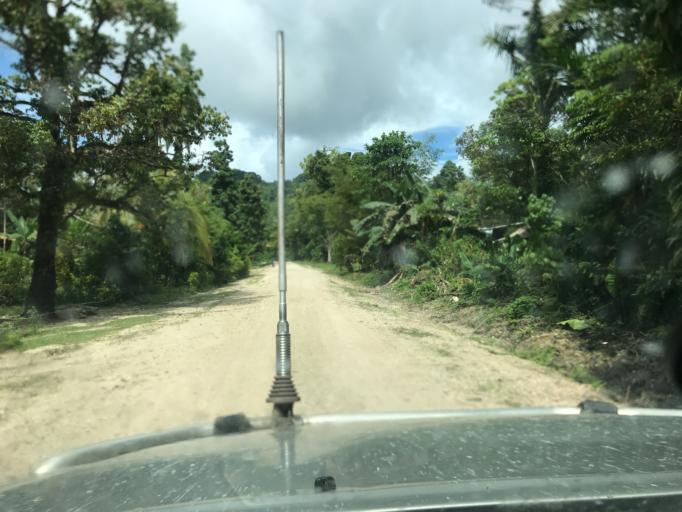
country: SB
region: Malaita
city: Auki
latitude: -8.4200
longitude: 160.8060
